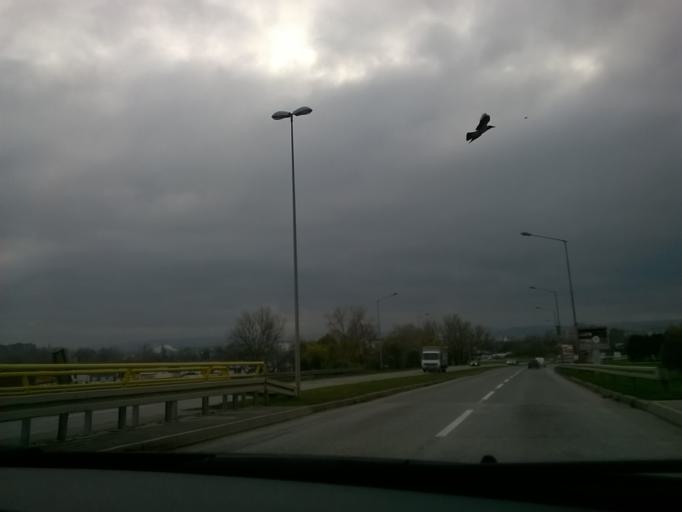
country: RS
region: Autonomna Pokrajina Vojvodina
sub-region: Juznobacki Okrug
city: Novi Sad
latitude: 45.2733
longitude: 19.8482
